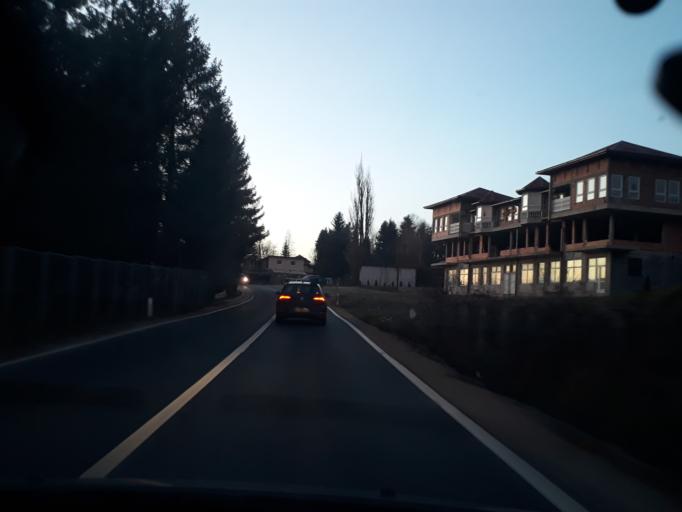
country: BA
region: Federation of Bosnia and Herzegovina
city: Hadzici
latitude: 43.8856
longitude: 18.1903
